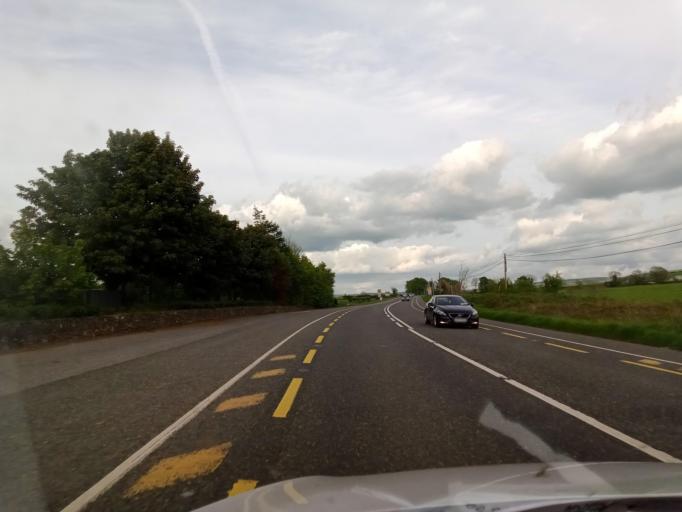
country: IE
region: Leinster
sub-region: Laois
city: Abbeyleix
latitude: 52.8582
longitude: -7.3812
